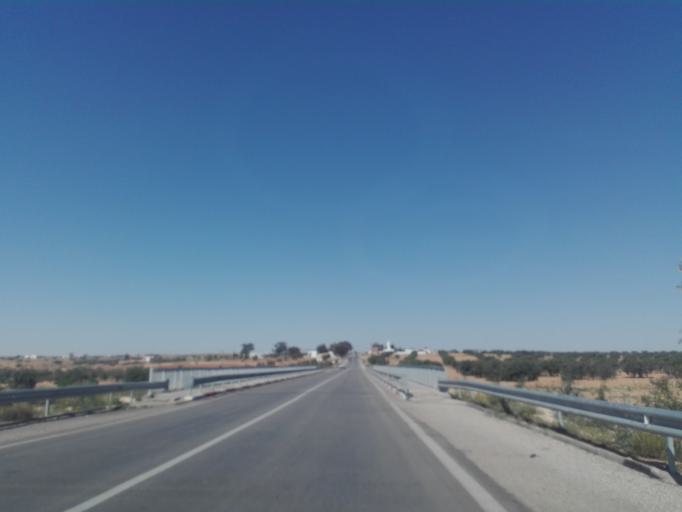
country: TN
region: Safaqis
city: Bi'r `Ali Bin Khalifah
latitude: 34.7412
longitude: 10.3783
